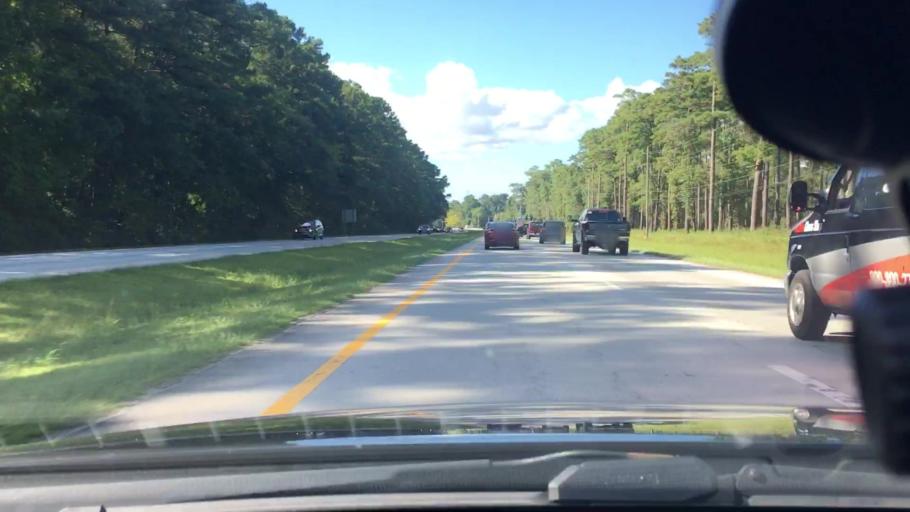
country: US
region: North Carolina
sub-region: Craven County
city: Neuse Forest
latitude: 34.9920
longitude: -76.9831
